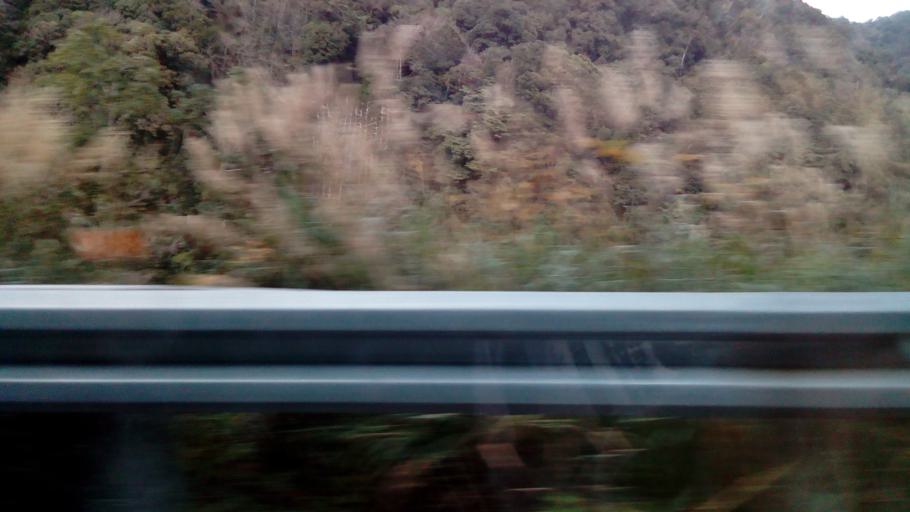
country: TW
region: Taiwan
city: Daxi
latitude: 24.4068
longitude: 121.3590
